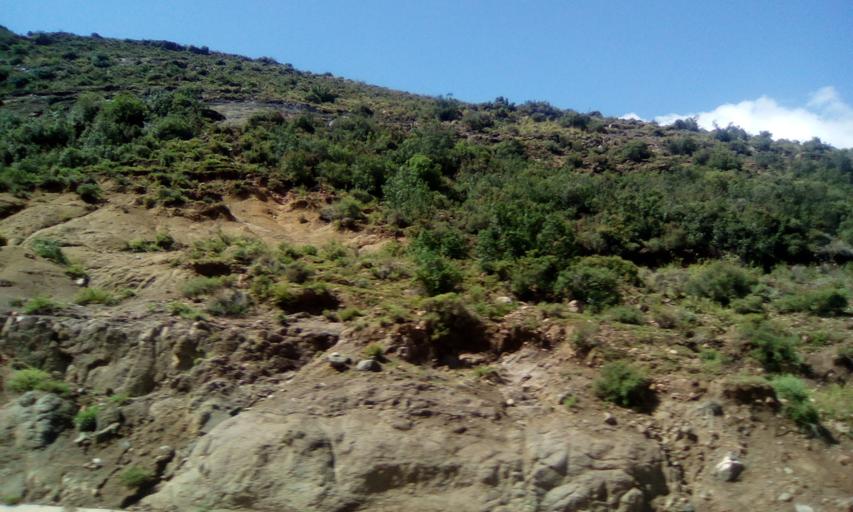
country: LS
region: Maseru
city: Nako
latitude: -29.6565
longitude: 27.8445
